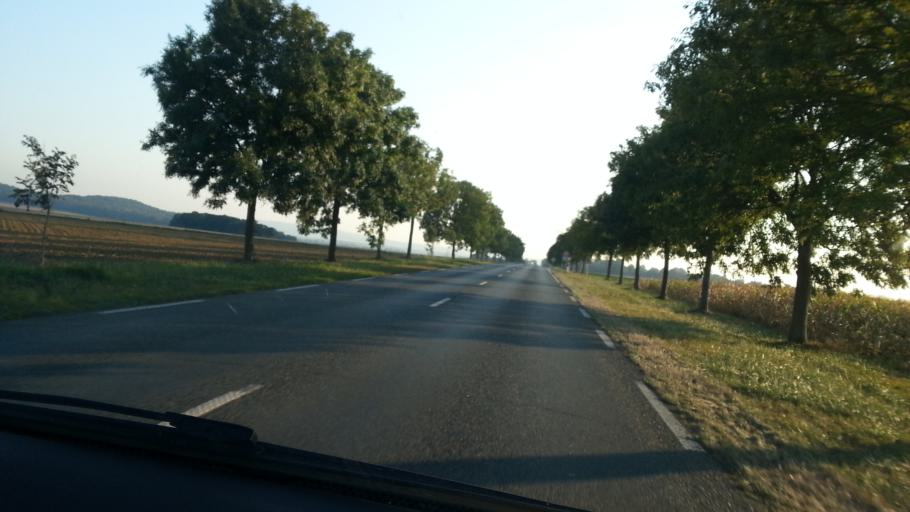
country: FR
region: Picardie
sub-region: Departement de l'Oise
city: Estrees-Saint-Denis
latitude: 49.3958
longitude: 2.6239
